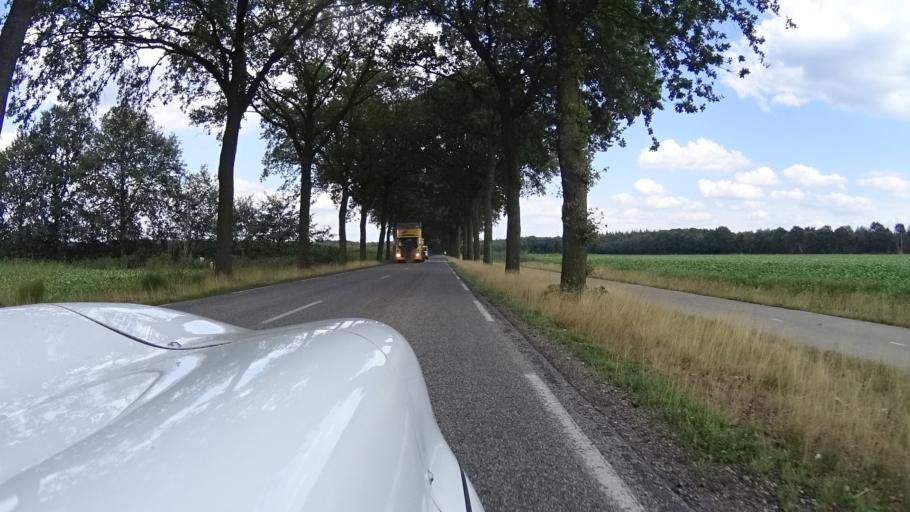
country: NL
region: North Brabant
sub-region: Gemeente Mill en Sint Hubert
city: Wilbertoord
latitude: 51.6281
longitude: 5.8111
